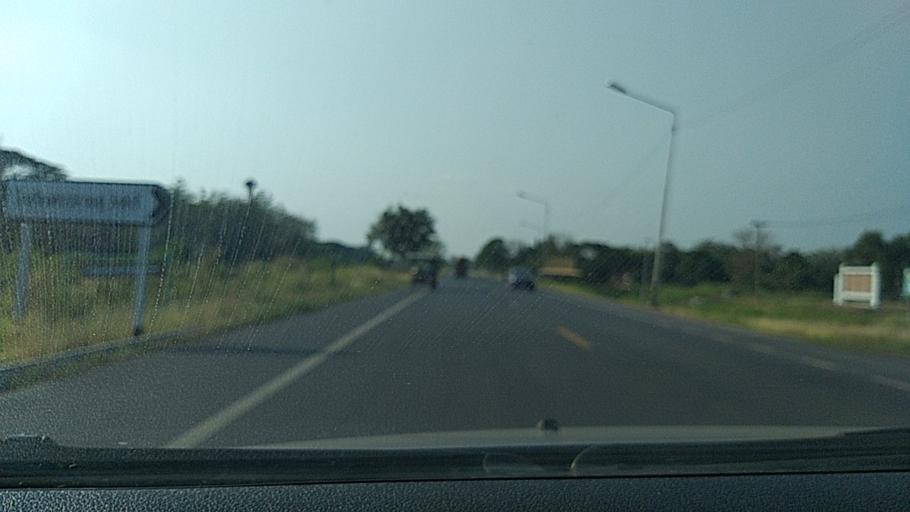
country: TH
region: Sing Buri
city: Phrom Buri
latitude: 14.7988
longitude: 100.4401
